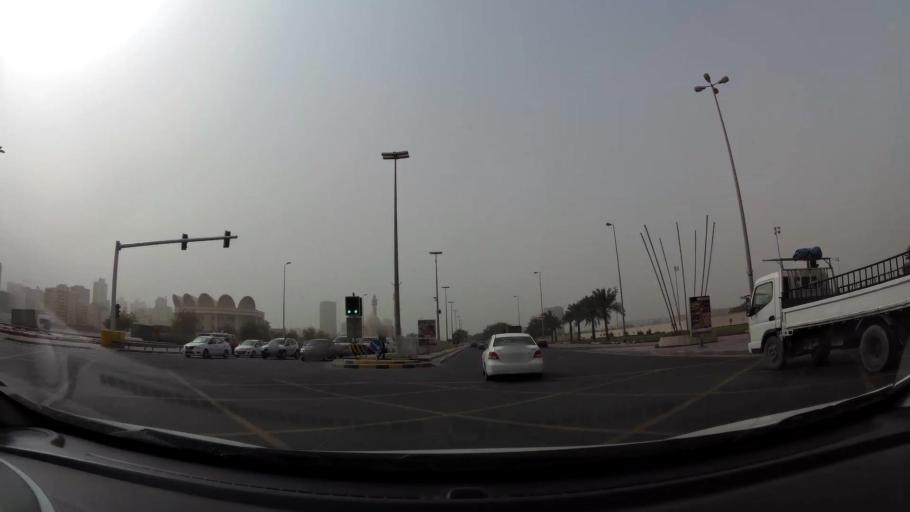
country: BH
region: Manama
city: Manama
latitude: 26.2241
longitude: 50.5979
